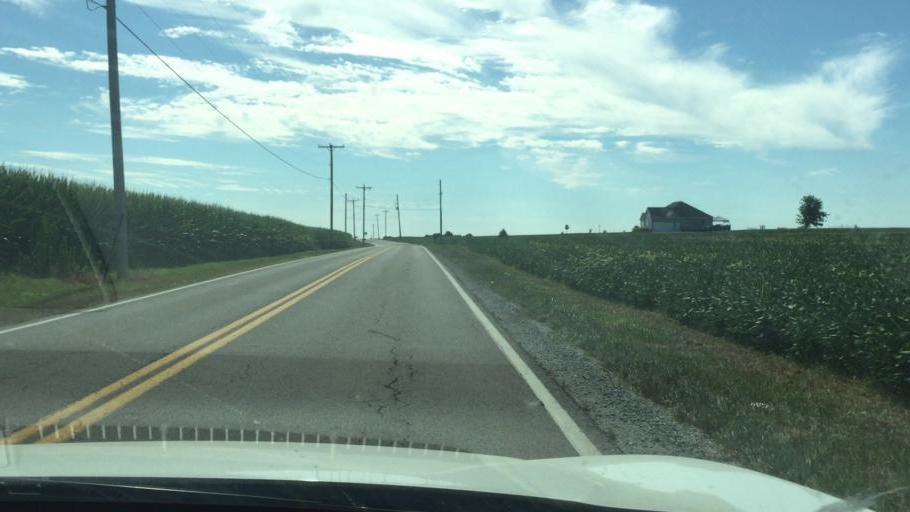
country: US
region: Ohio
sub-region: Clark County
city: Lisbon
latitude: 39.9419
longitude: -83.6413
